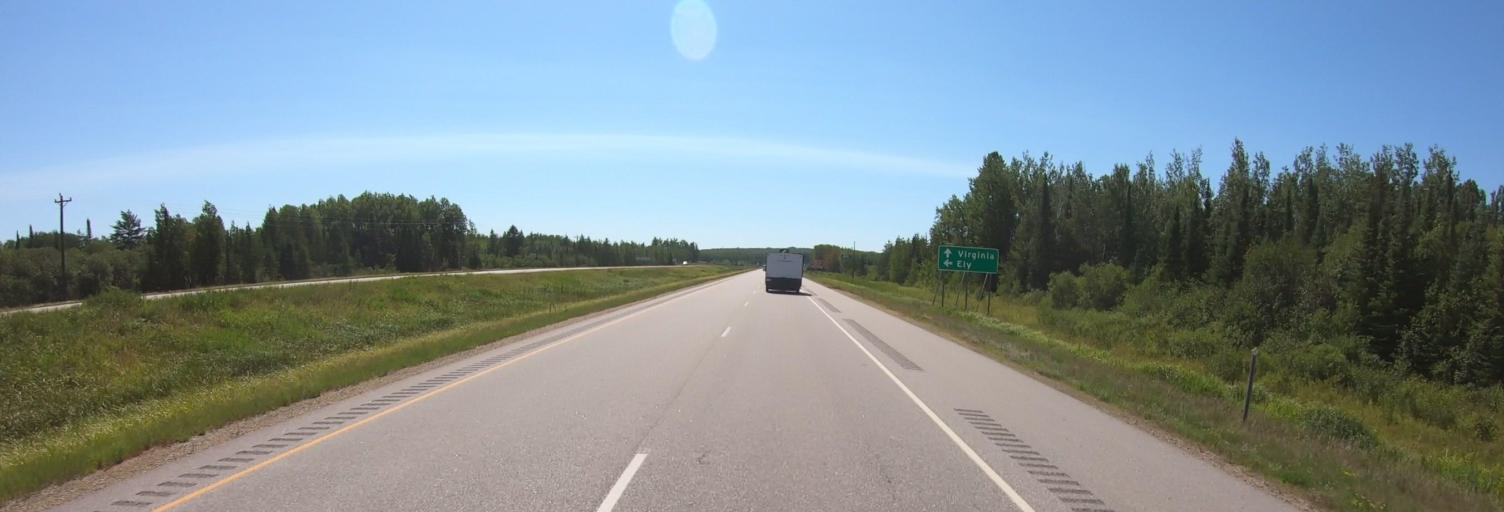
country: US
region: Minnesota
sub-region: Saint Louis County
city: Mountain Iron
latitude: 47.7856
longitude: -92.6599
